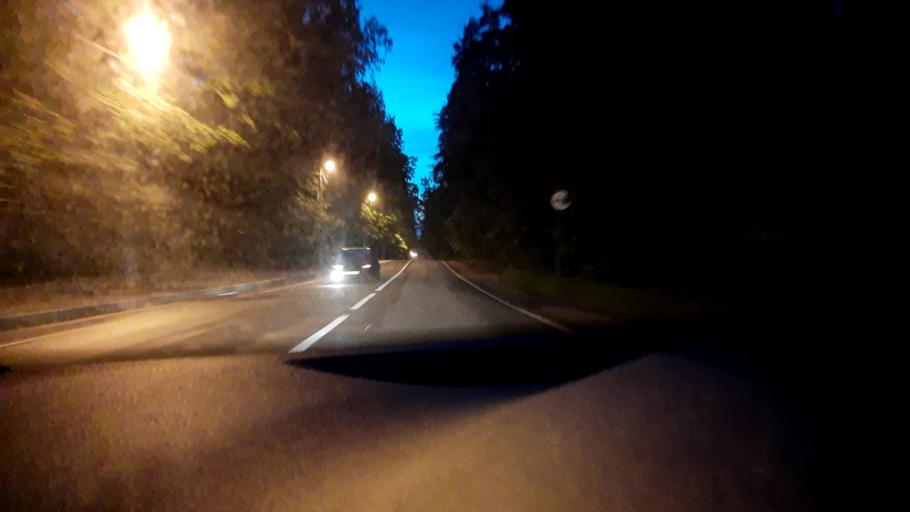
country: RU
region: Moskovskaya
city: Petrovo-Dal'neye
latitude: 55.7922
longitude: 37.2043
